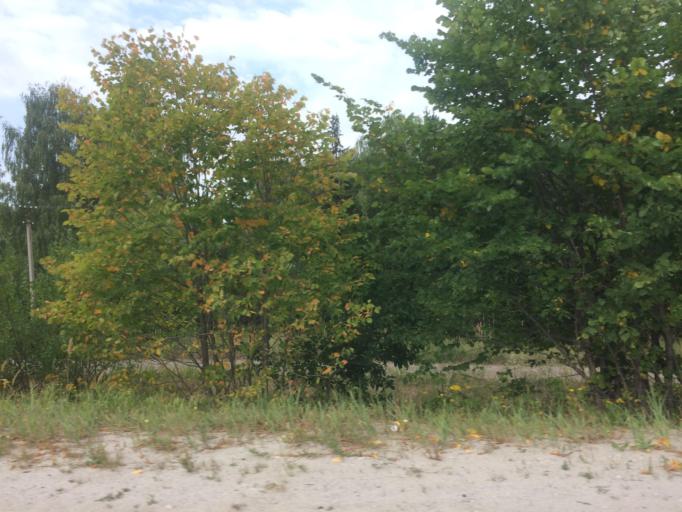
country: RU
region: Mariy-El
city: Yoshkar-Ola
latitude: 56.5444
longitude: 47.9807
